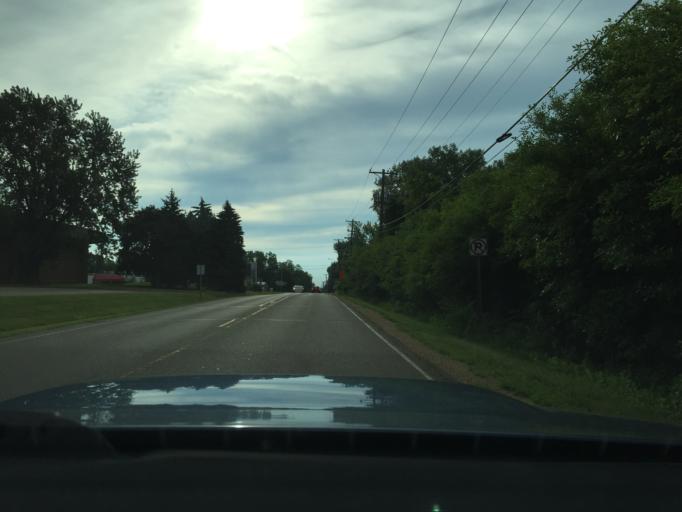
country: US
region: Minnesota
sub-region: Dakota County
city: West Saint Paul
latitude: 44.8980
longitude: -93.0979
